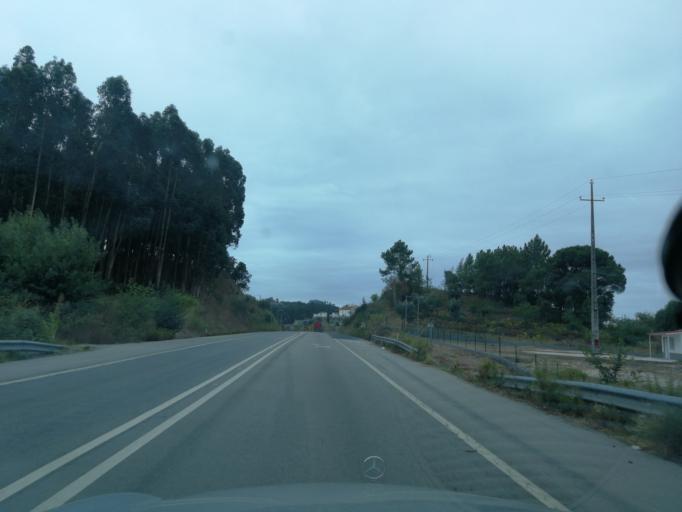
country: PT
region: Aveiro
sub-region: Agueda
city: Valongo
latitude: 40.6389
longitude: -8.4693
